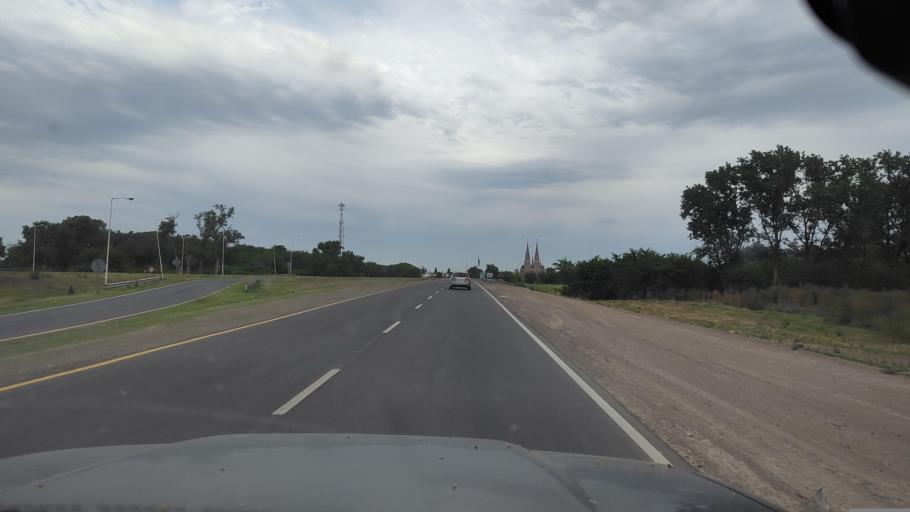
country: AR
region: Buenos Aires
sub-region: Partido de Lujan
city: Lujan
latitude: -34.5504
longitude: -59.1159
